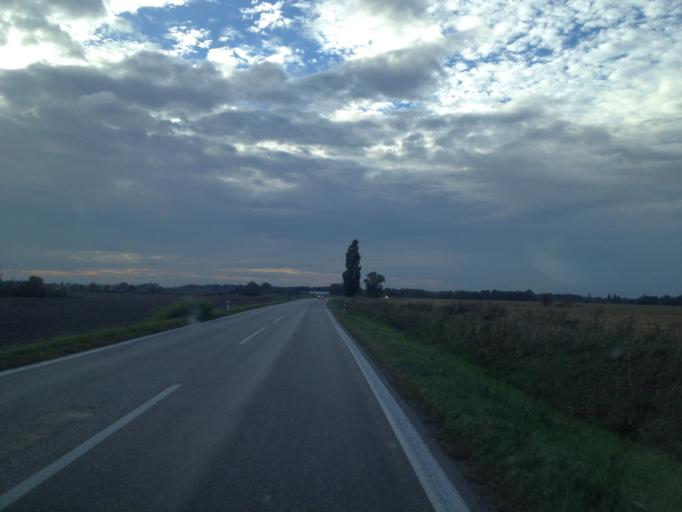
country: SK
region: Nitriansky
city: Komarno
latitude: 47.7632
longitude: 18.1788
